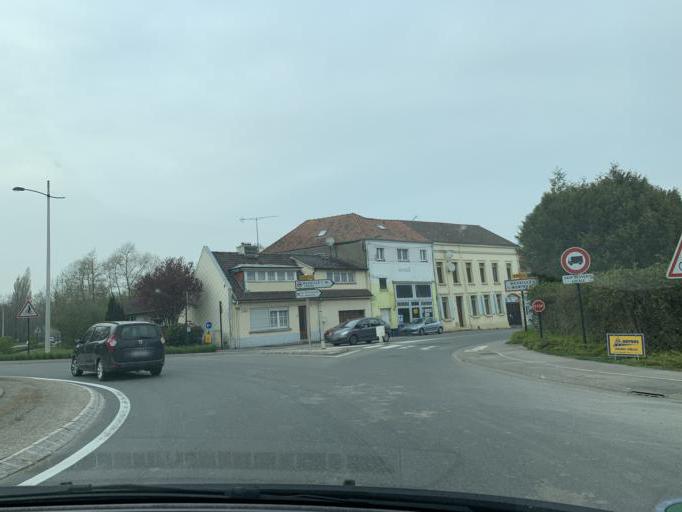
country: FR
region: Nord-Pas-de-Calais
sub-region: Departement du Pas-de-Calais
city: Montreuil
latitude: 50.4717
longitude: 1.7730
